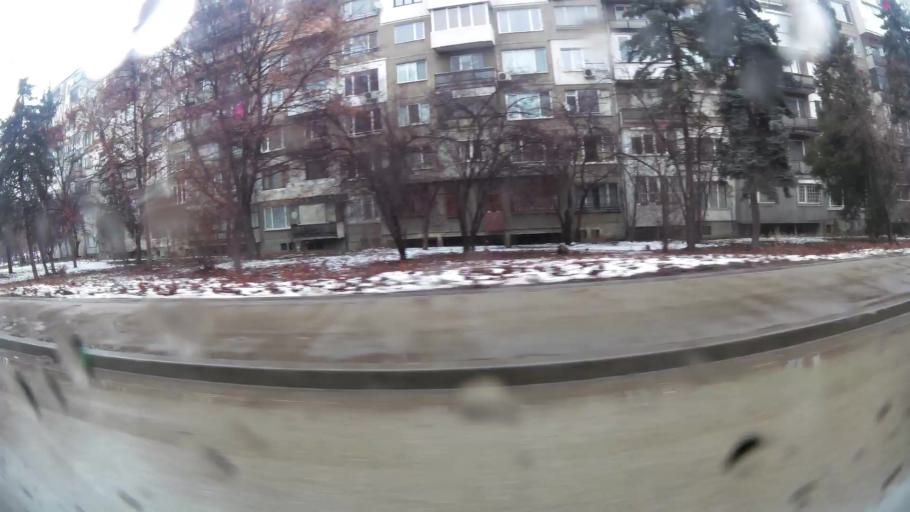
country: BG
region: Sofia-Capital
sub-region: Stolichna Obshtina
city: Sofia
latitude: 42.6659
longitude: 23.2862
